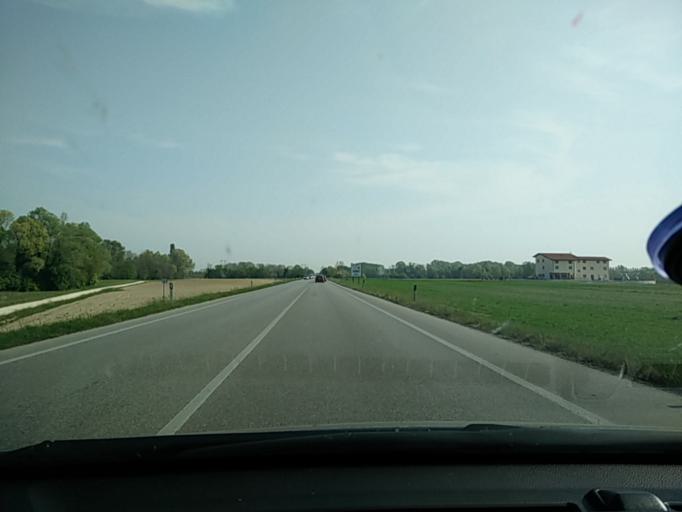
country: IT
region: Friuli Venezia Giulia
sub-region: Provincia di Pordenone
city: Prata di Sotto
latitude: 45.9069
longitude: 12.6194
